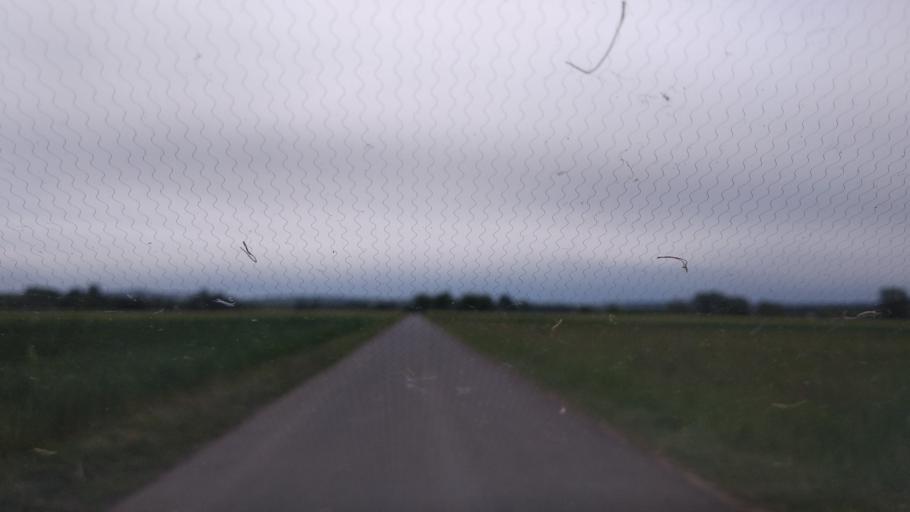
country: DE
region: North Rhine-Westphalia
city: Borgentreich
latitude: 51.5562
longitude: 9.1924
